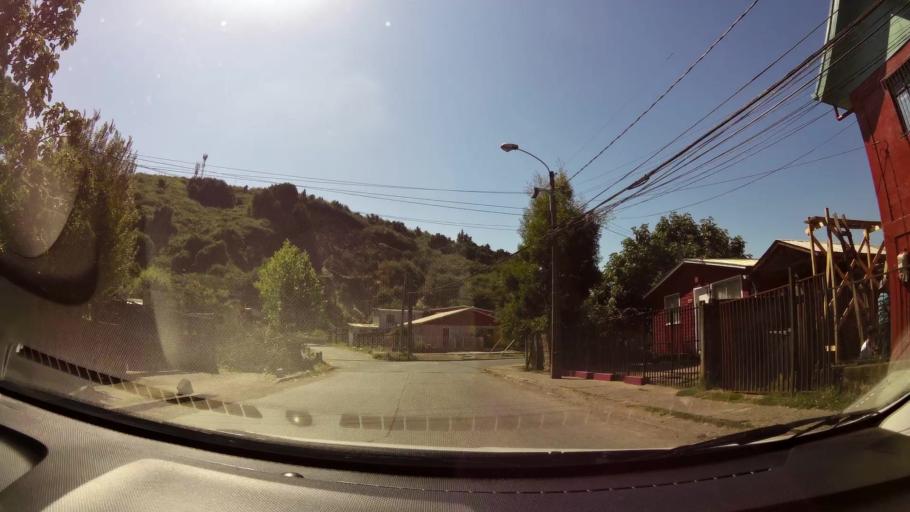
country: CL
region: Biobio
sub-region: Provincia de Concepcion
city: Concepcion
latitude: -36.7975
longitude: -73.0380
